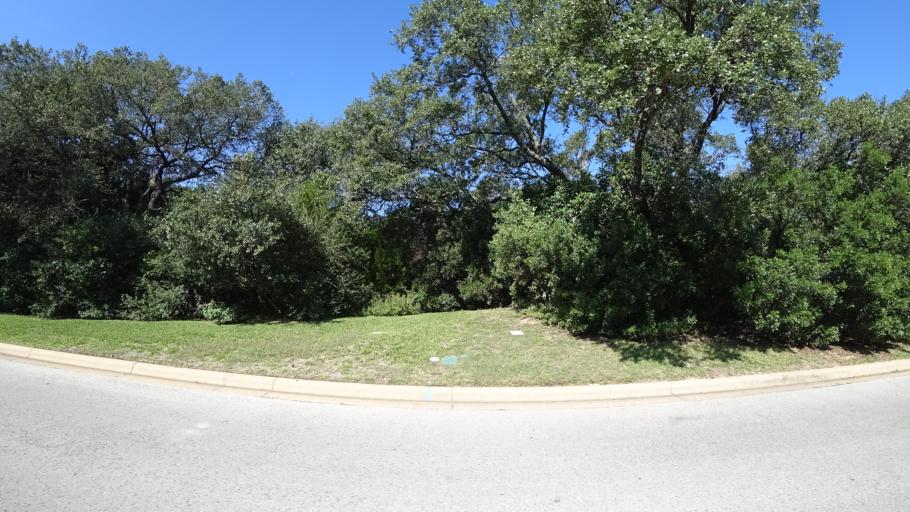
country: US
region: Texas
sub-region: Travis County
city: Rollingwood
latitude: 30.2796
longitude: -97.7948
